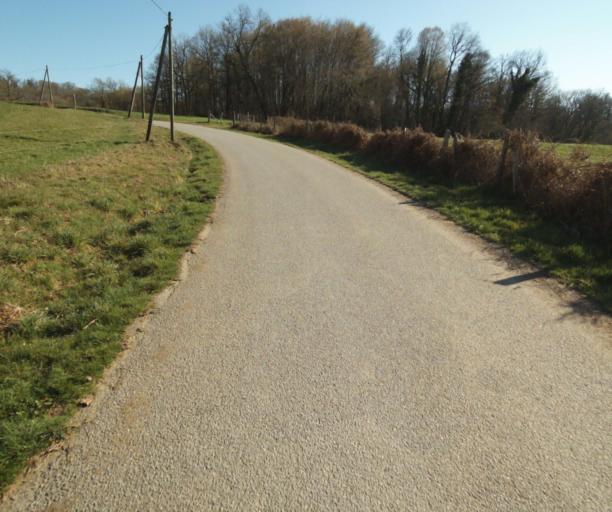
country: FR
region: Limousin
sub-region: Departement de la Correze
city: Chamboulive
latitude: 45.4771
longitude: 1.6911
